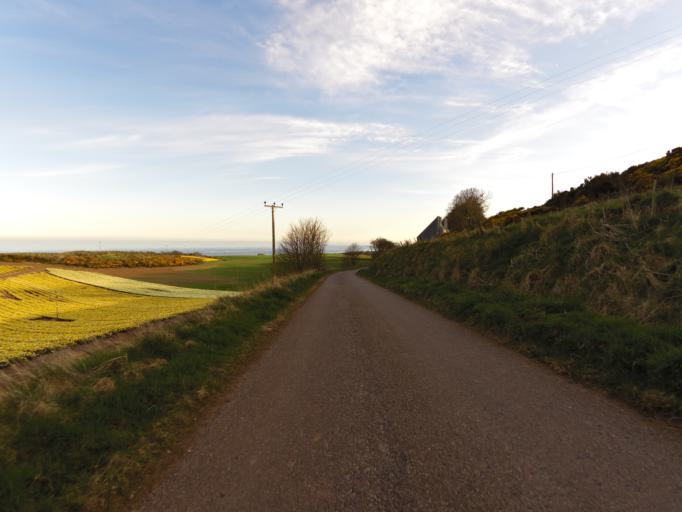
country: GB
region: Scotland
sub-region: Aberdeenshire
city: Inverbervie
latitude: 56.8723
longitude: -2.2355
